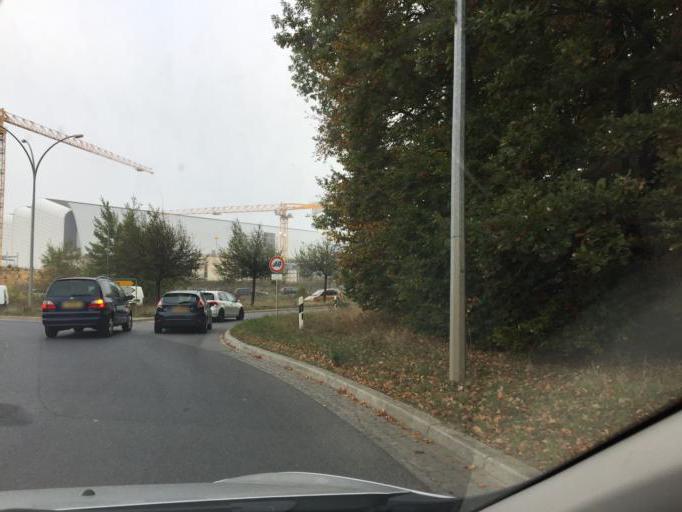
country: LU
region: Luxembourg
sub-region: Canton de Luxembourg
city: Sandweiler
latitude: 49.6135
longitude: 6.2007
